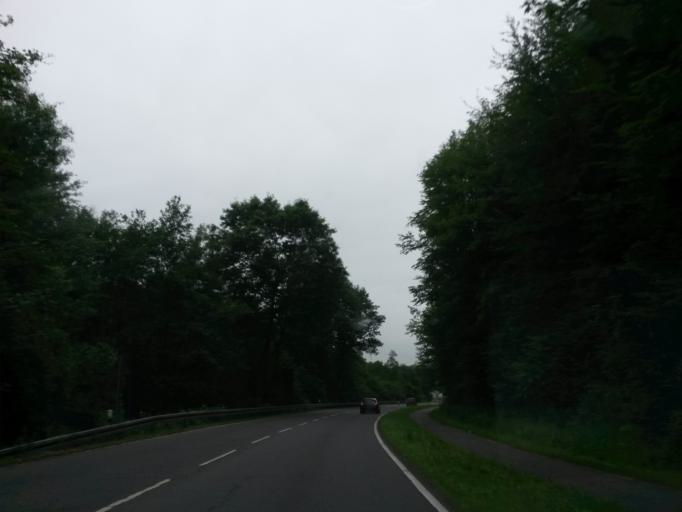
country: DE
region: North Rhine-Westphalia
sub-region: Regierungsbezirk Koln
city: Gummersbach
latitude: 51.0219
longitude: 7.5556
